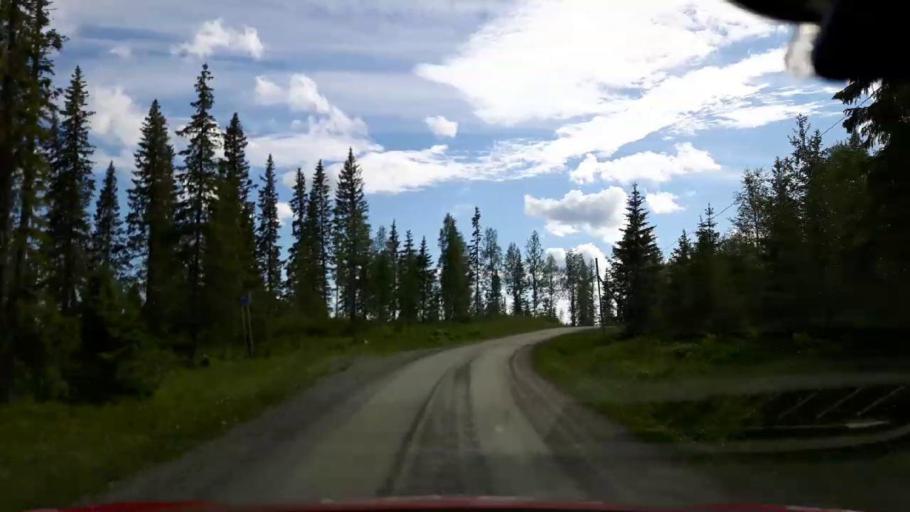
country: SE
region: Jaemtland
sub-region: Krokoms Kommun
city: Valla
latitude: 63.8440
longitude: 14.0761
